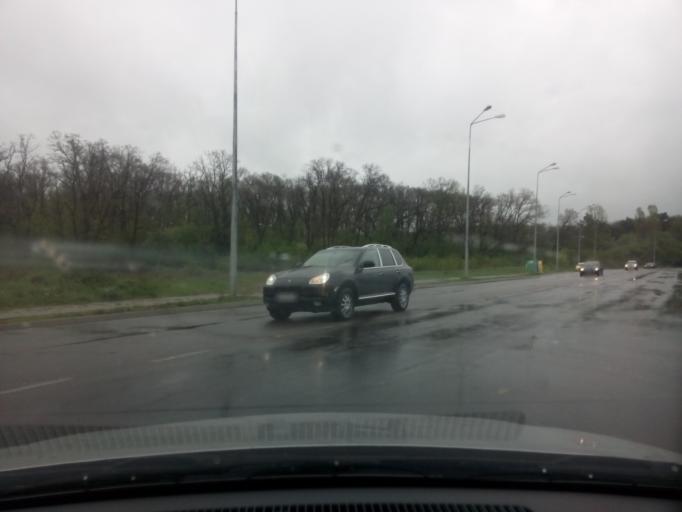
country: RO
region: Ilfov
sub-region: Comuna Otopeni
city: Otopeni
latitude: 44.5158
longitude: 26.0875
